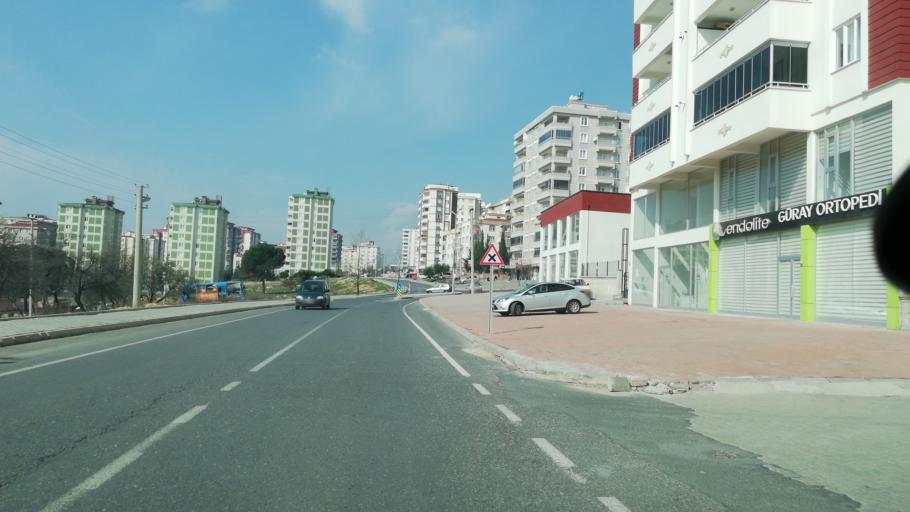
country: TR
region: Kahramanmaras
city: Kahramanmaras
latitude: 37.5886
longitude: 36.8637
